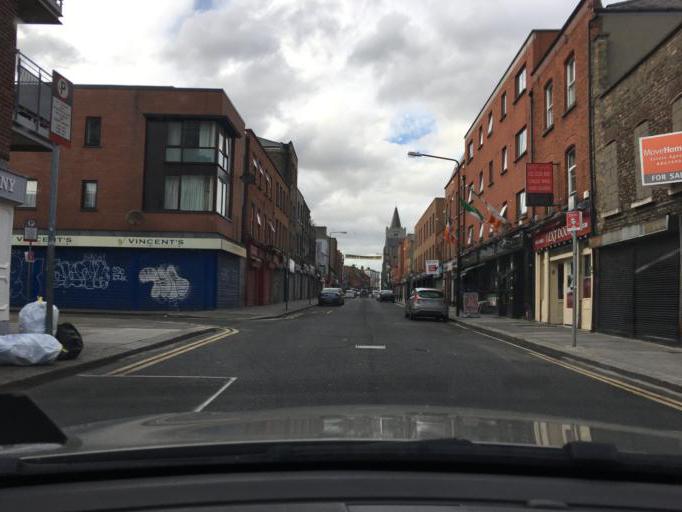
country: IE
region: Leinster
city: Rialto
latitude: 53.3403
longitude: -6.2781
